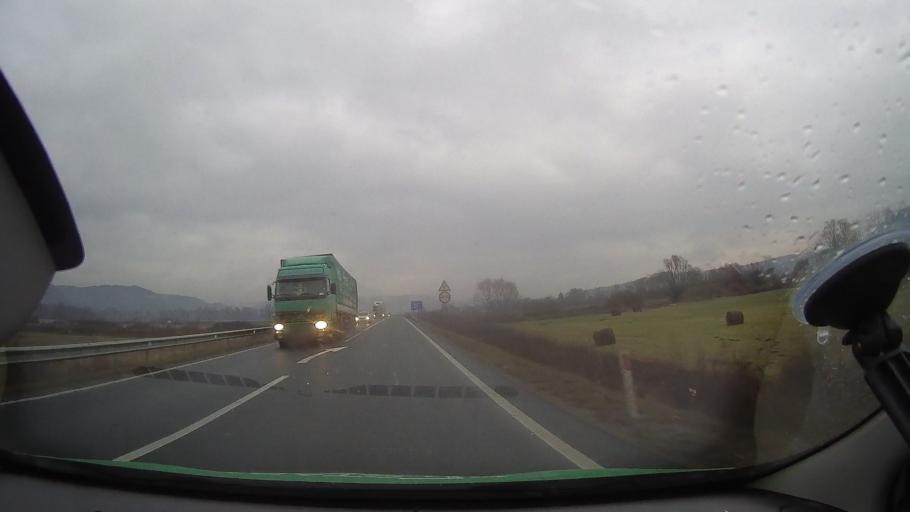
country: RO
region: Hunedoara
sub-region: Comuna Baia de Cris
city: Baia de Cris
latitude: 46.1808
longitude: 22.6759
